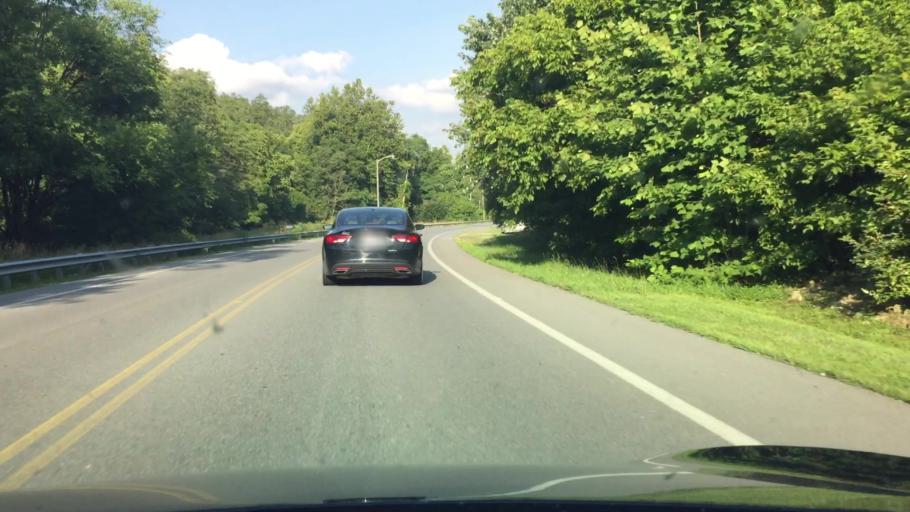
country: US
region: Virginia
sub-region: City of Radford
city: Radford
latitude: 37.1182
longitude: -80.5477
